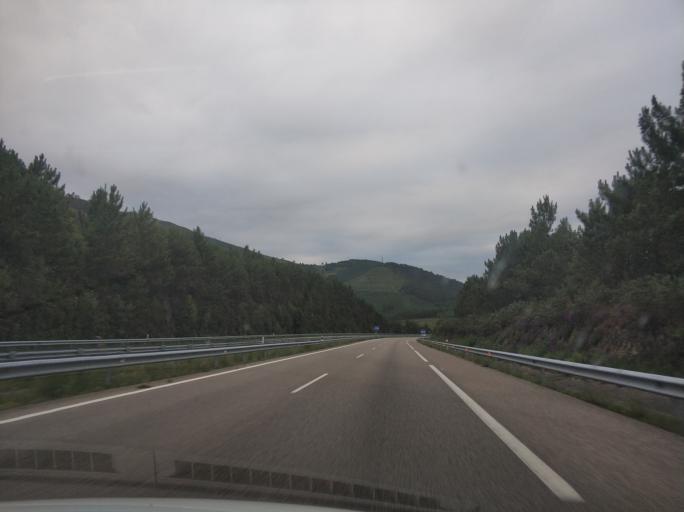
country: ES
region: Asturias
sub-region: Province of Asturias
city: Tineo
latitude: 43.5360
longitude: -6.4832
